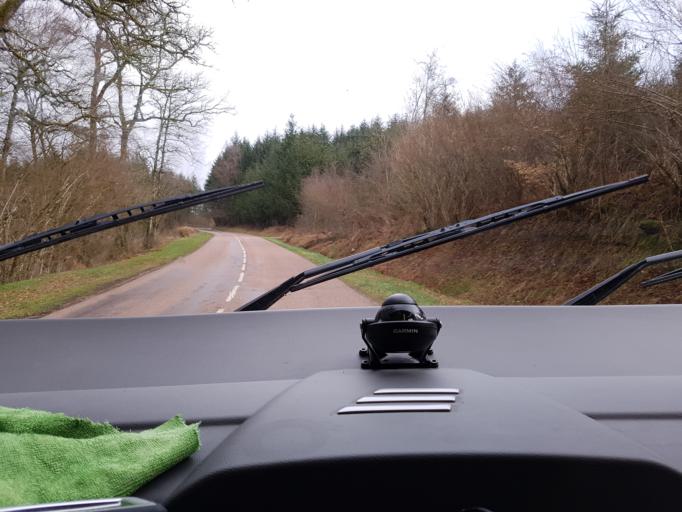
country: FR
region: Bourgogne
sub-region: Departement de la Nievre
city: Chateau-Chinon(Ville)
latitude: 47.2235
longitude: 4.0324
